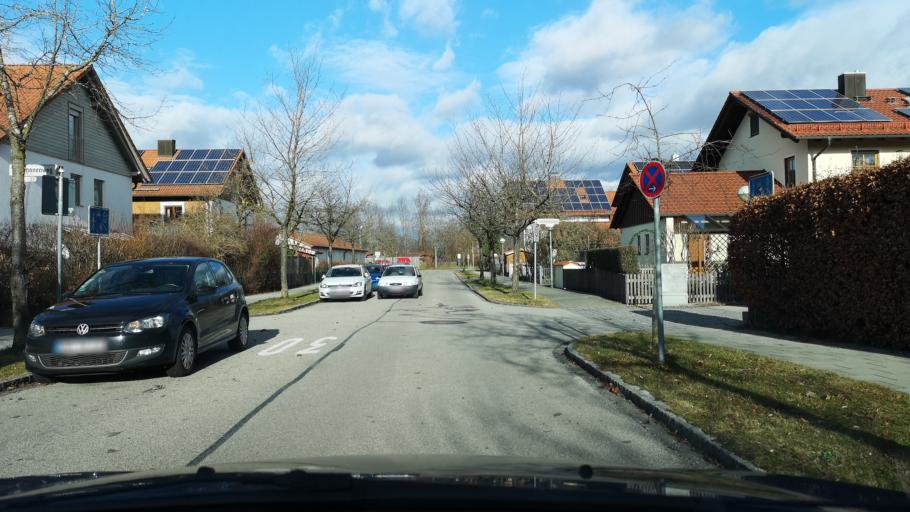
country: DE
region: Bavaria
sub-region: Upper Bavaria
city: Poing
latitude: 48.1793
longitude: 11.8053
